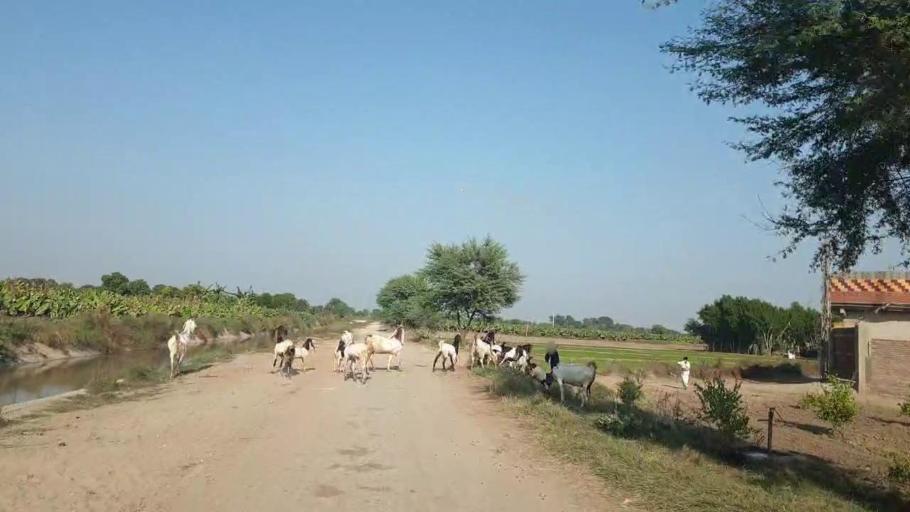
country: PK
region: Sindh
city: Matiari
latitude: 25.5393
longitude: 68.4430
